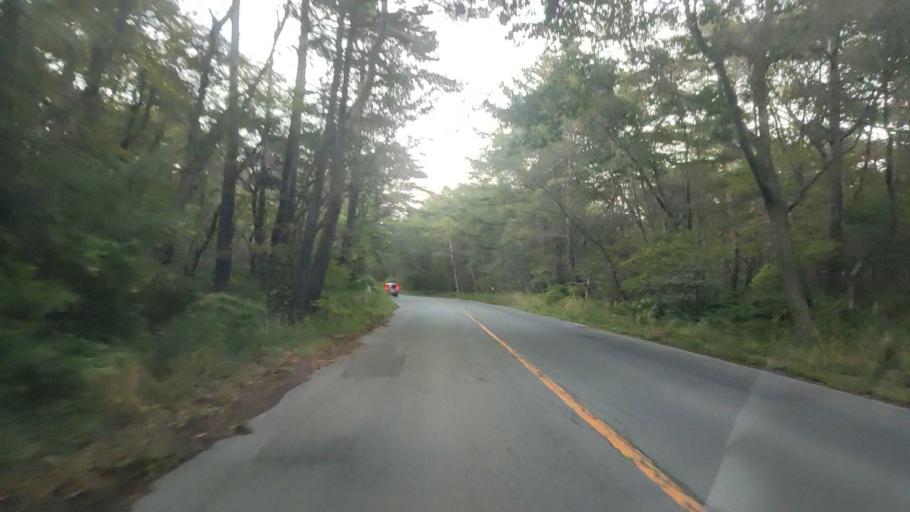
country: JP
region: Nagano
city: Komoro
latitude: 36.4176
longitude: 138.5704
